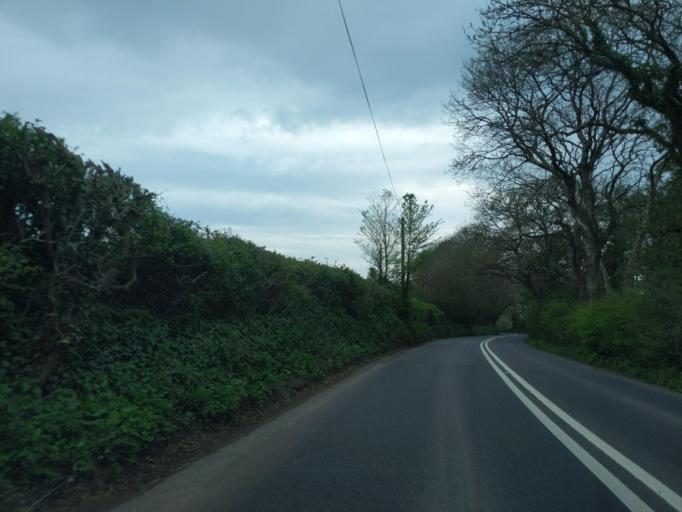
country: GB
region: England
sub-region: Devon
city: Crediton
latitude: 50.7999
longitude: -3.7033
